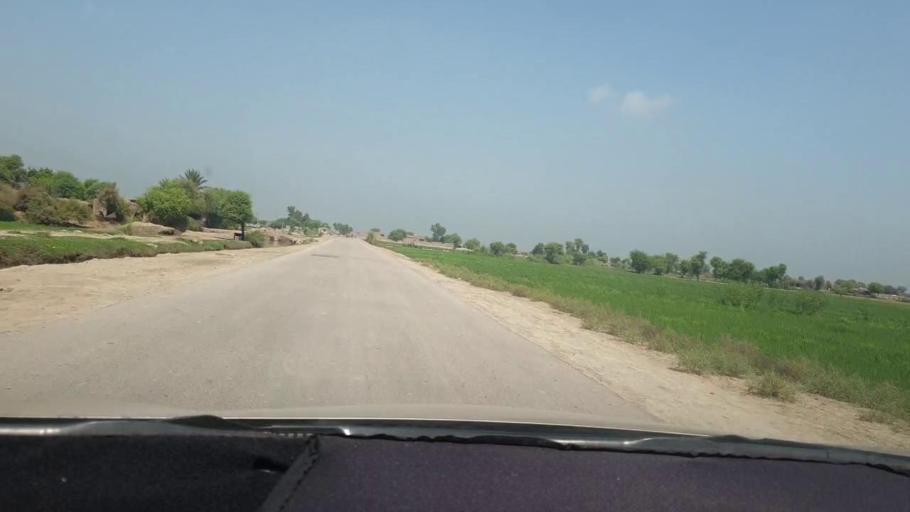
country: PK
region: Sindh
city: Miro Khan
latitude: 27.7829
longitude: 68.0528
